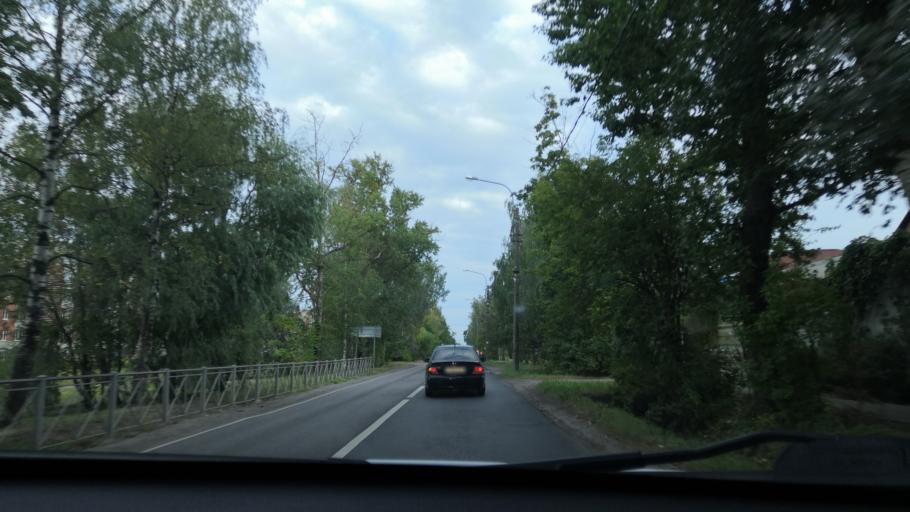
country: RU
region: St.-Petersburg
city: Pushkin
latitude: 59.6991
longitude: 30.4100
